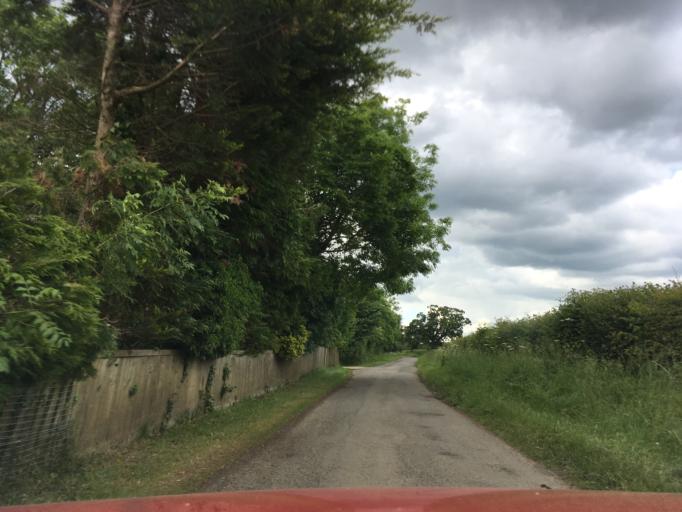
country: GB
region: England
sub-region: Gloucestershire
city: Coates
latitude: 51.6643
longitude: -2.0178
